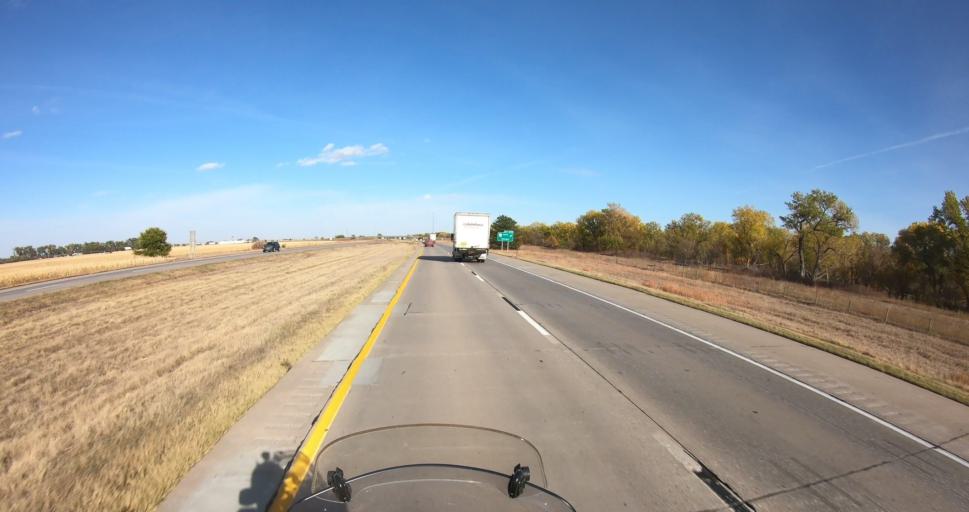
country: US
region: Nebraska
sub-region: Buffalo County
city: Kearney
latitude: 40.6837
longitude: -98.9631
